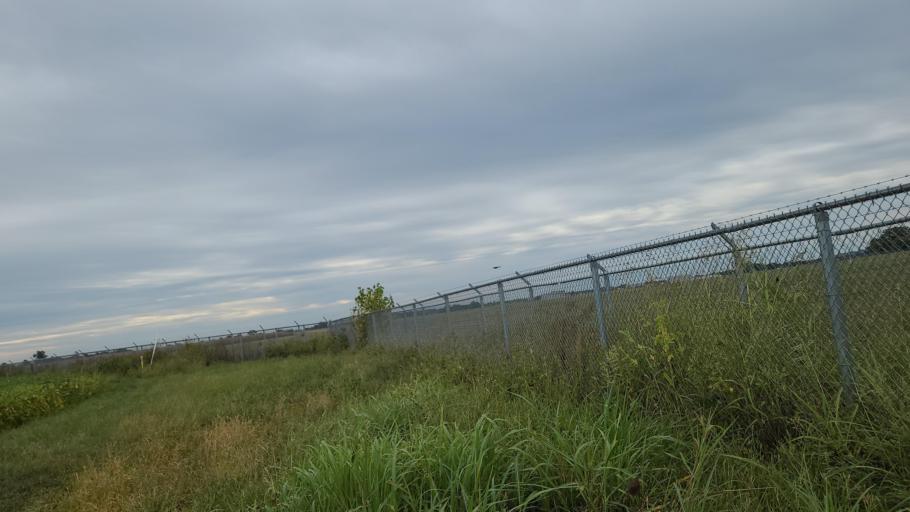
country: US
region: Kansas
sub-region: Douglas County
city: Lawrence
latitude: 39.0166
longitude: -95.2157
